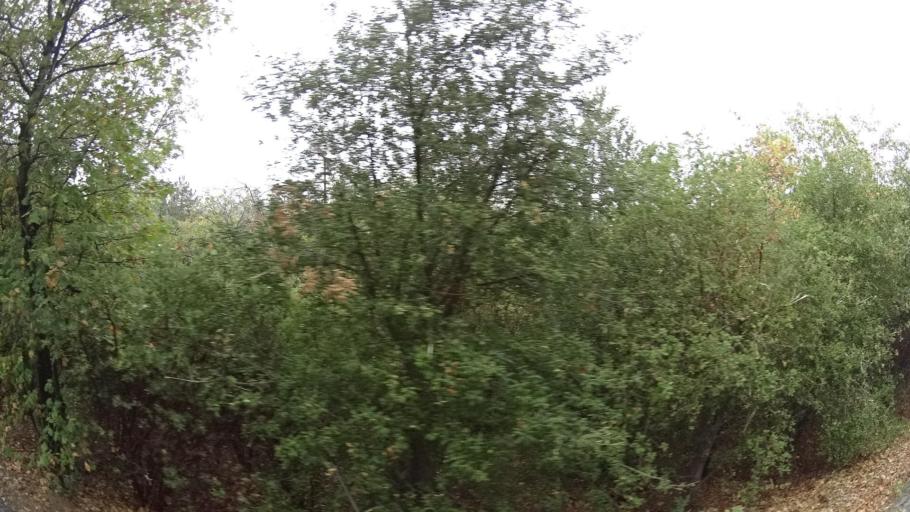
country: US
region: California
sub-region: San Diego County
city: Julian
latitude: 33.0556
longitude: -116.6026
